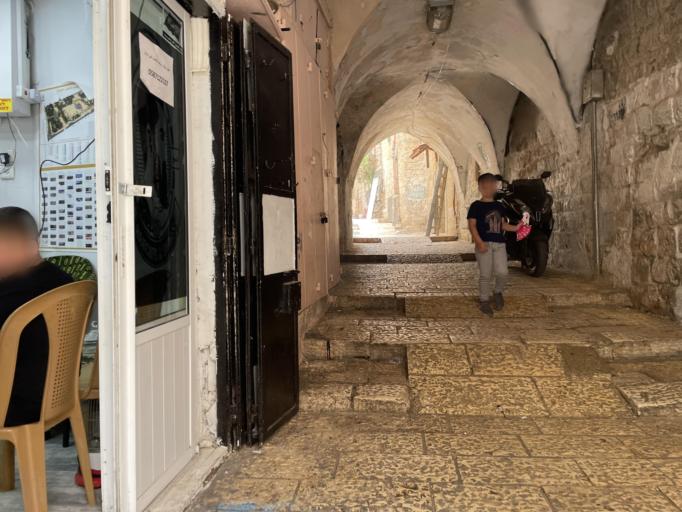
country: PS
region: West Bank
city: East Jerusalem
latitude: 31.7811
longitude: 35.2334
